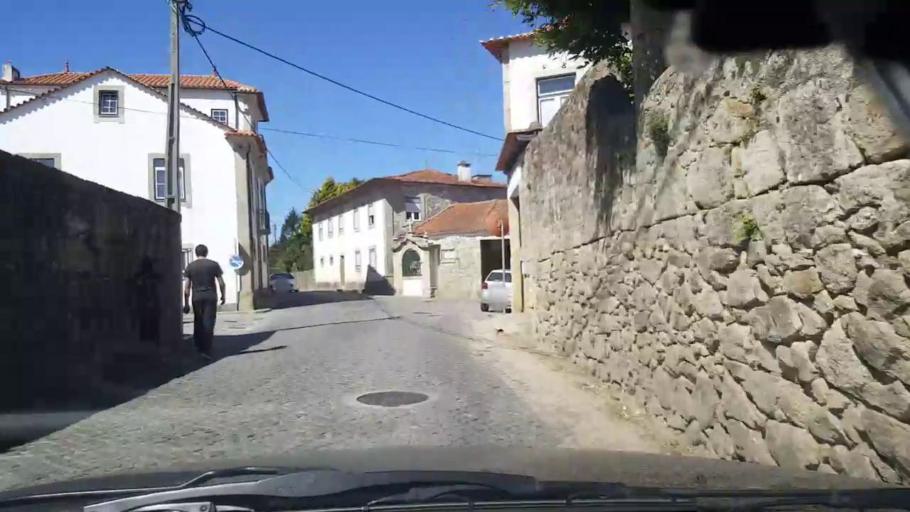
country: PT
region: Porto
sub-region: Vila do Conde
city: Arvore
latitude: 41.3234
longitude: -8.7030
